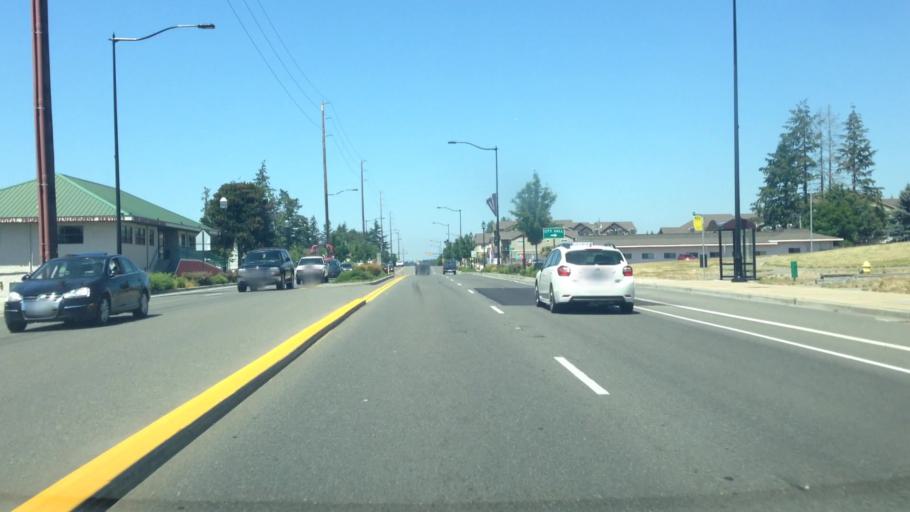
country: US
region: Washington
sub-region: Pierce County
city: Edgewood
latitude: 47.2362
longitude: -122.2939
